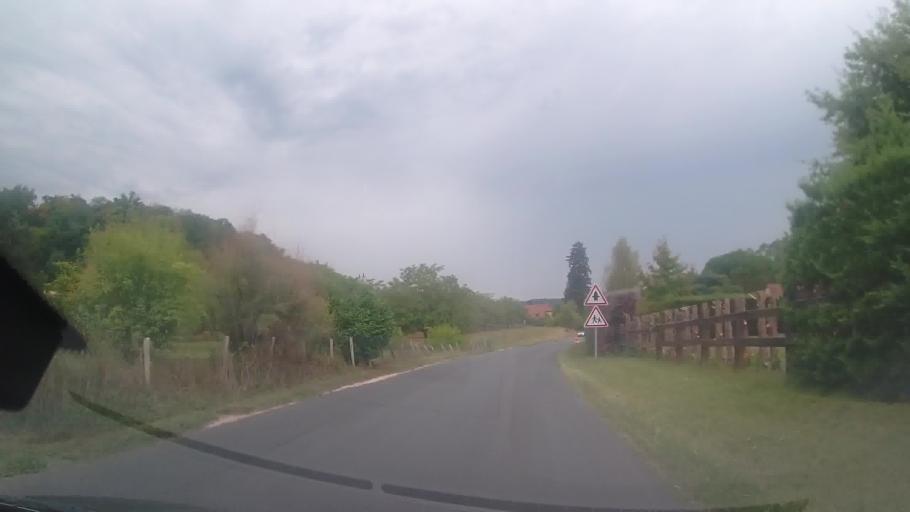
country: FR
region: Aquitaine
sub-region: Departement de la Dordogne
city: Carsac-Aillac
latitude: 44.8377
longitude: 1.2832
